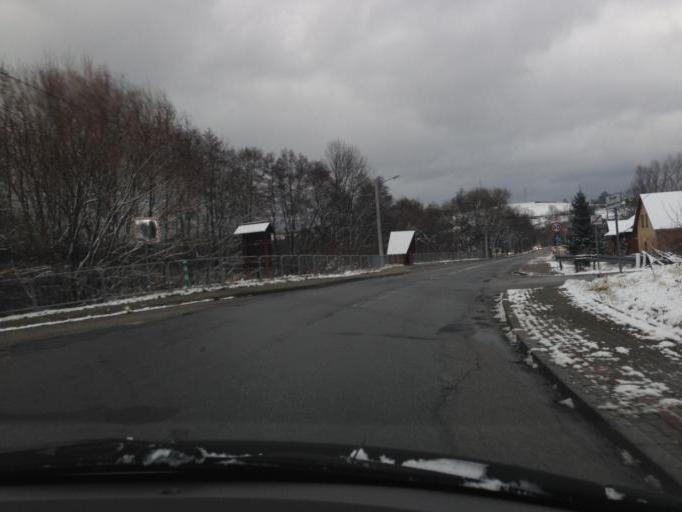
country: PL
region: Lesser Poland Voivodeship
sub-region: Powiat brzeski
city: Iwkowa
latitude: 49.8584
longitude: 20.5566
